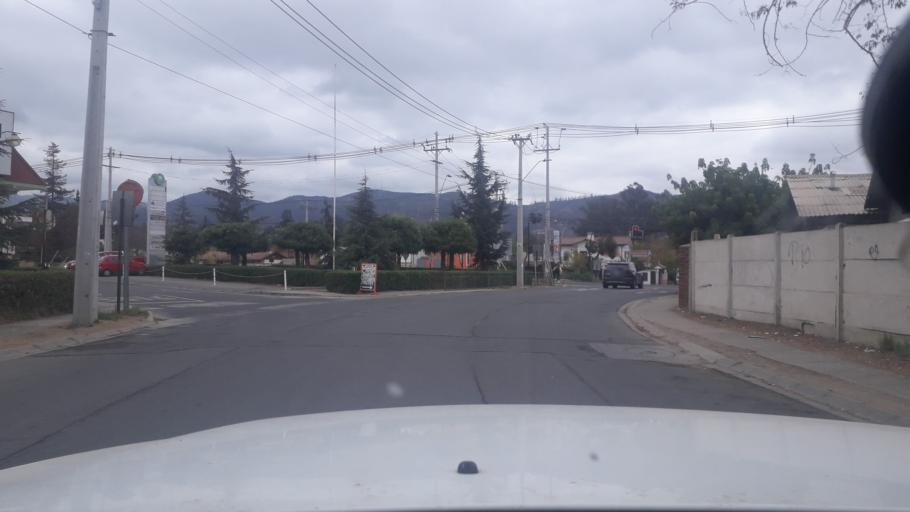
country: CL
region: Valparaiso
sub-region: Provincia de Marga Marga
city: Villa Alemana
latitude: -33.0512
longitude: -71.3379
